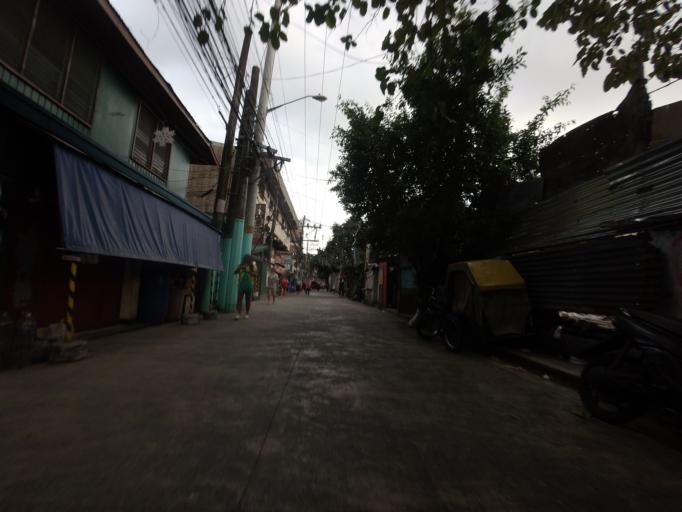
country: PH
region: Metro Manila
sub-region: Makati City
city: Makati City
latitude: 14.5554
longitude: 120.9942
